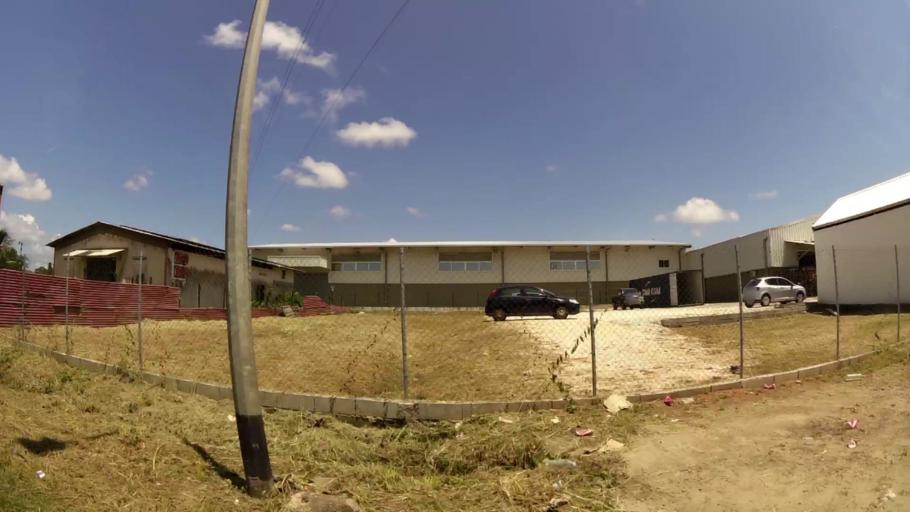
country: GF
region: Guyane
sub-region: Guyane
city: Cayenne
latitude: 4.9017
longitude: -52.3176
